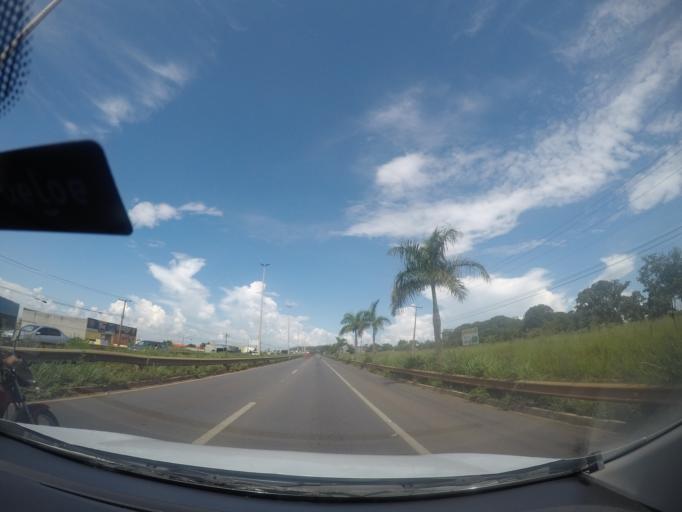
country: BR
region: Goias
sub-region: Goiania
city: Goiania
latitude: -16.6586
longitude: -49.3702
